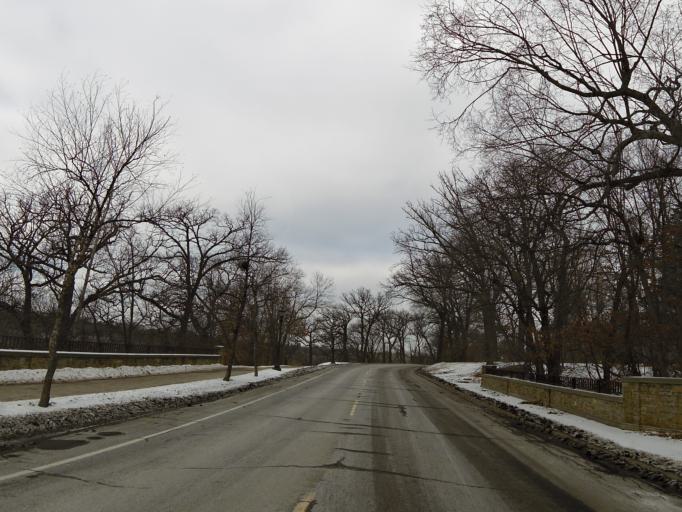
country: US
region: Minnesota
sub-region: Ramsey County
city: Lauderdale
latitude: 44.9325
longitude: -93.1981
